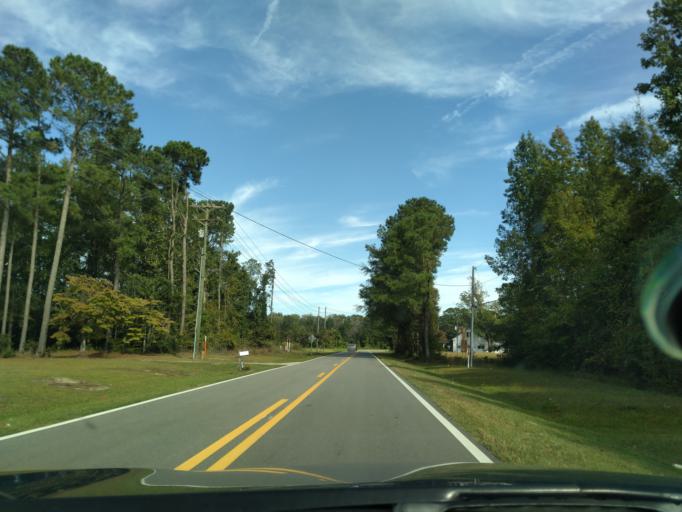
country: US
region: North Carolina
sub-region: Beaufort County
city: River Road
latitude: 35.5055
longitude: -76.9794
